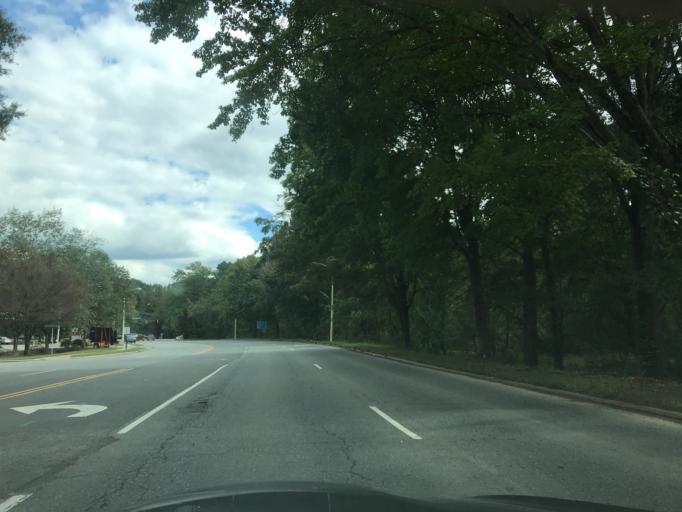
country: US
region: North Carolina
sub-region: Orange County
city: Chapel Hill
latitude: 35.9258
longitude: -79.0271
